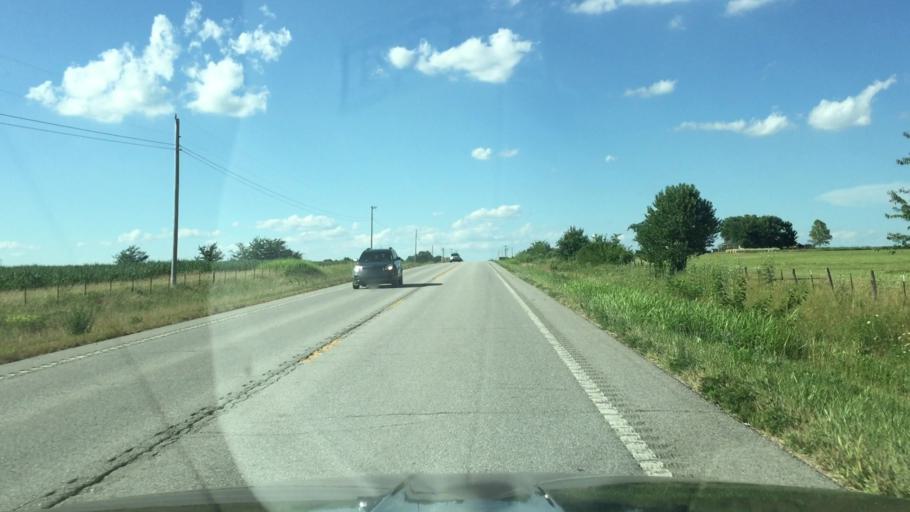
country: US
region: Missouri
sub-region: Morgan County
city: Versailles
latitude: 38.4544
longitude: -92.8091
